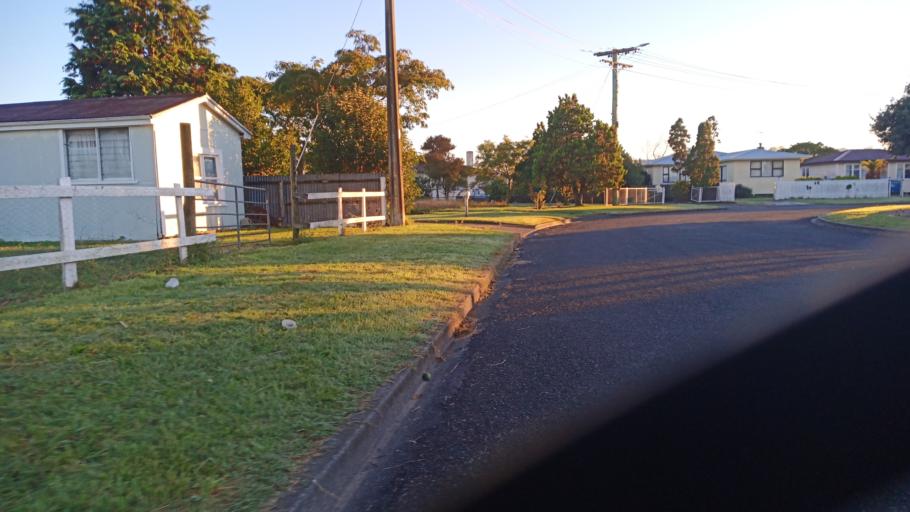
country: NZ
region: Gisborne
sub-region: Gisborne District
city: Gisborne
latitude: -38.6606
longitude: 177.9905
